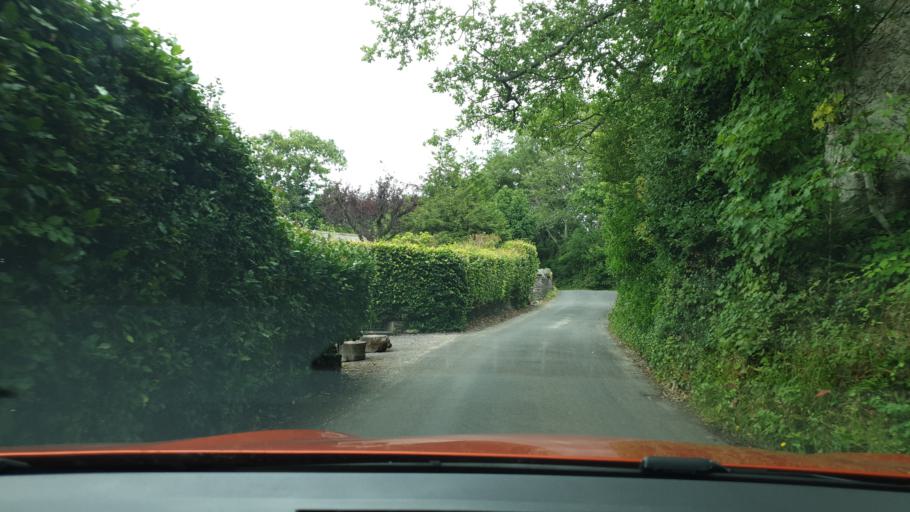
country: GB
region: England
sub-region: Cumbria
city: Penrith
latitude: 54.5813
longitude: -2.8526
